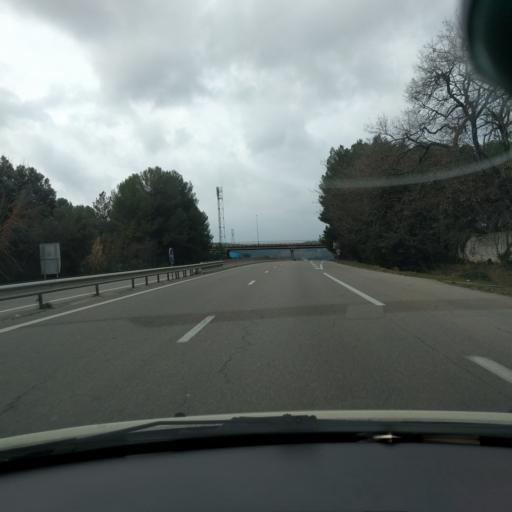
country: FR
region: Provence-Alpes-Cote d'Azur
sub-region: Departement des Bouches-du-Rhone
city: Simiane-Collongue
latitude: 43.4369
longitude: 5.4282
